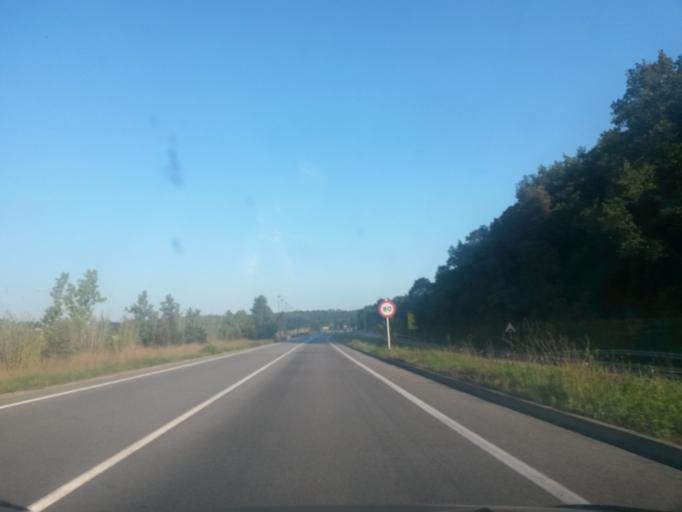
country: ES
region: Catalonia
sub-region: Provincia de Girona
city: Besalu
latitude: 42.1925
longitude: 2.7287
